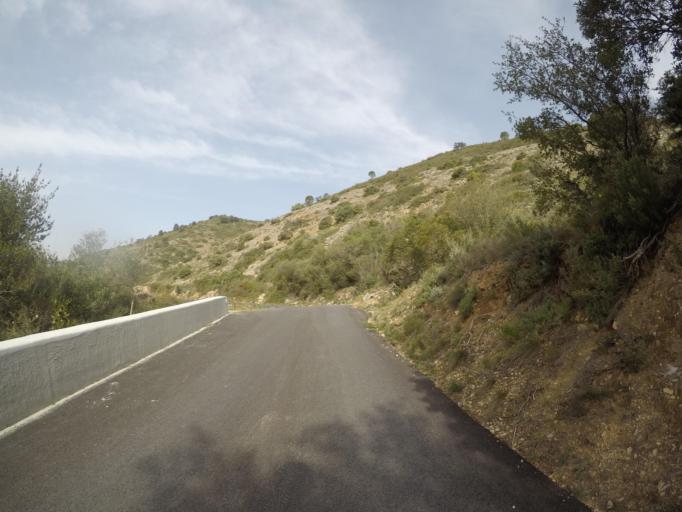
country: FR
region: Languedoc-Roussillon
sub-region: Departement des Pyrenees-Orientales
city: Estagel
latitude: 42.7800
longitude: 2.7252
